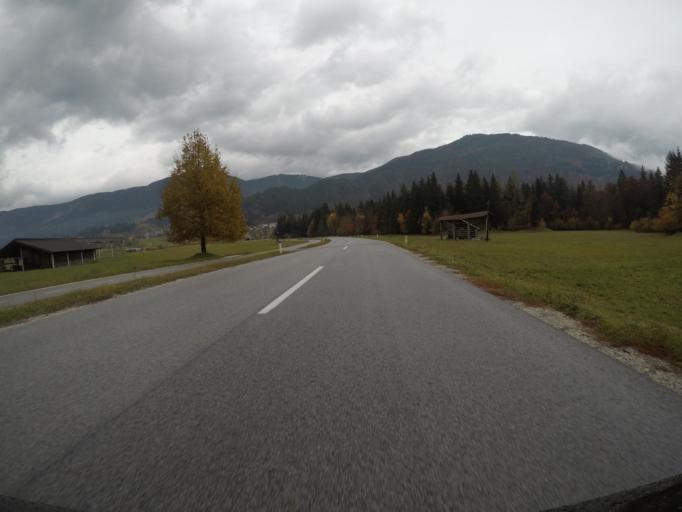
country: AT
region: Carinthia
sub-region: Politischer Bezirk Villach Land
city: Arnoldstein
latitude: 46.4884
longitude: 13.7240
